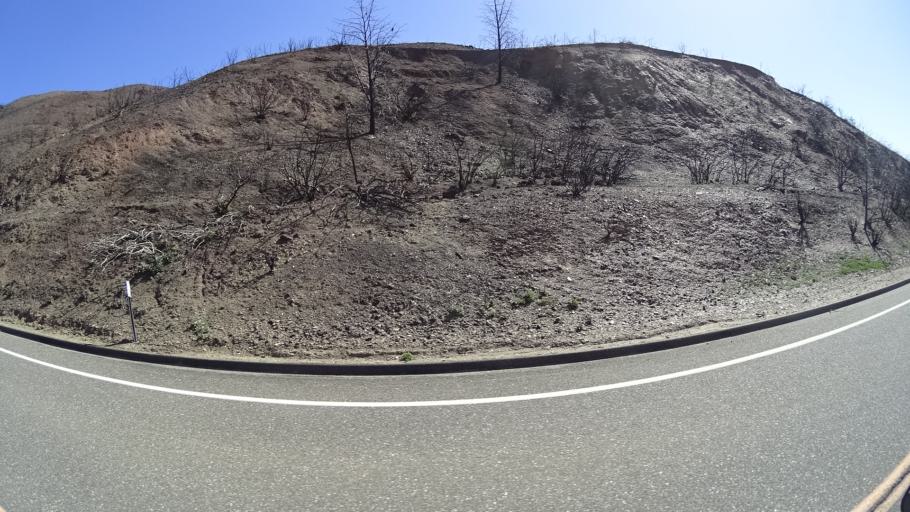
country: US
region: California
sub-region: Tehama County
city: Rancho Tehama Reserve
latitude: 39.6504
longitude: -122.6166
